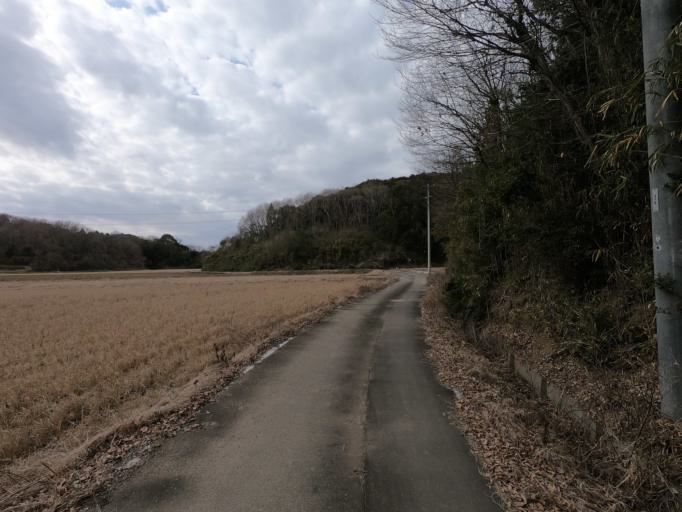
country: JP
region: Ibaraki
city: Inashiki
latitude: 36.0602
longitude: 140.4468
